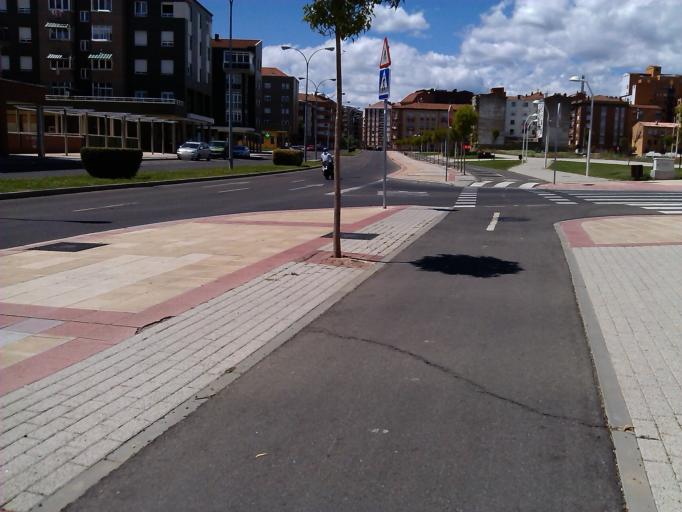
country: ES
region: Castille and Leon
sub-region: Provincia de Leon
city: Leon
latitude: 42.6022
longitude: -5.5575
